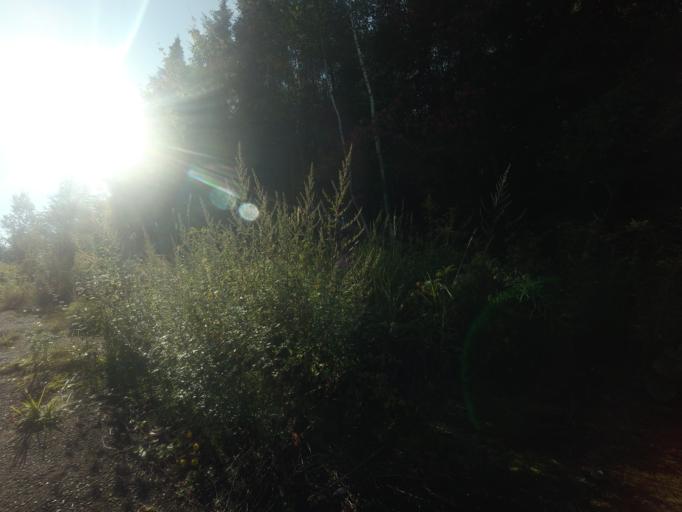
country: CA
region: Quebec
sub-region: Laurentides
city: Sainte-Agathe-des-Monts
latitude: 46.0475
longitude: -74.2677
